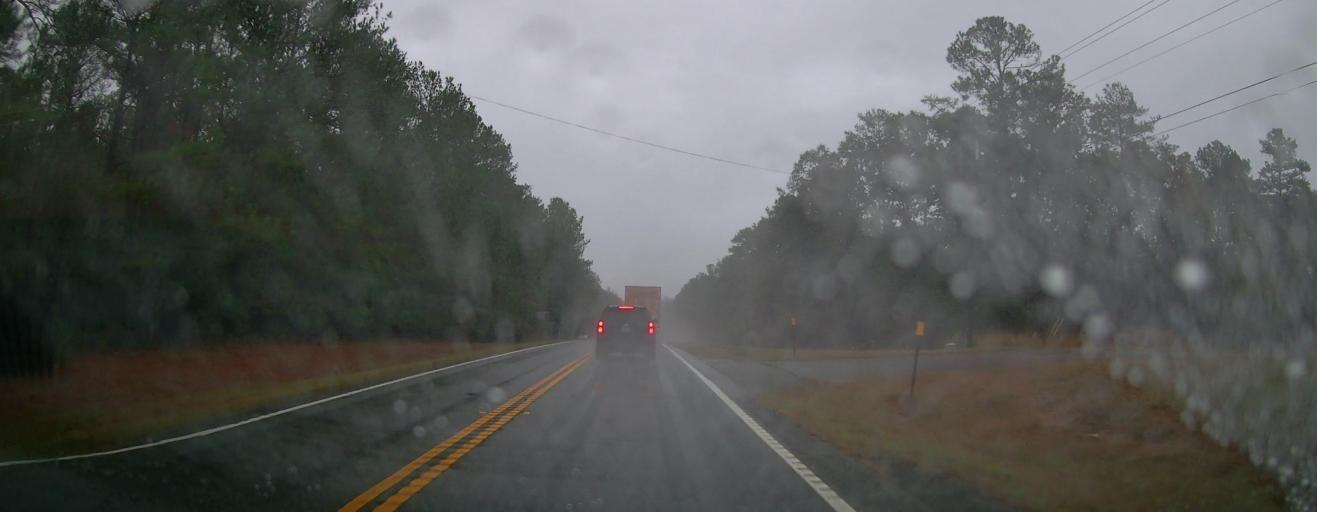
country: US
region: Georgia
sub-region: Jones County
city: Gray
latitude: 33.1147
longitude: -83.4795
